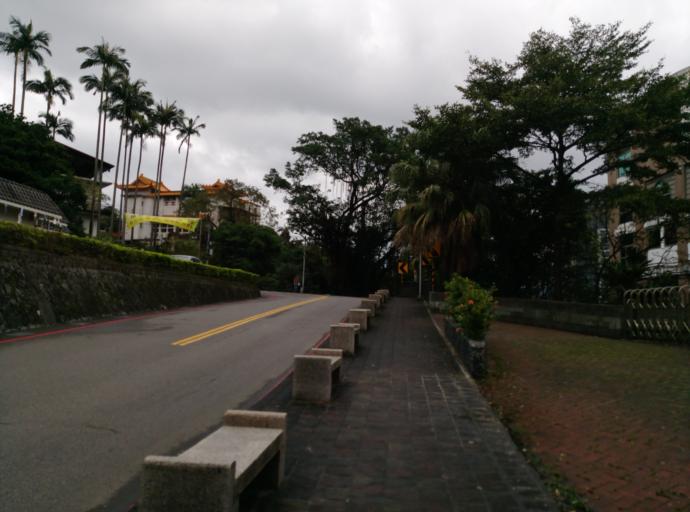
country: TW
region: Taiwan
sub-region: Keelung
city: Keelung
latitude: 25.1318
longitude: 121.7490
